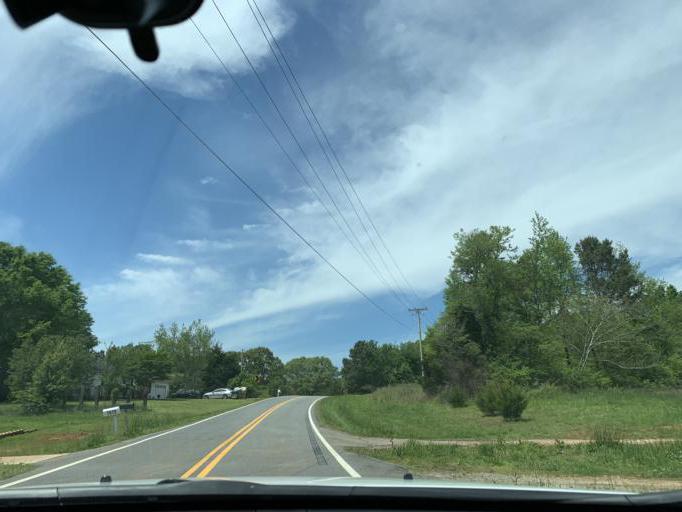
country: US
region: Georgia
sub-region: Hall County
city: Flowery Branch
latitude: 34.2653
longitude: -84.0222
